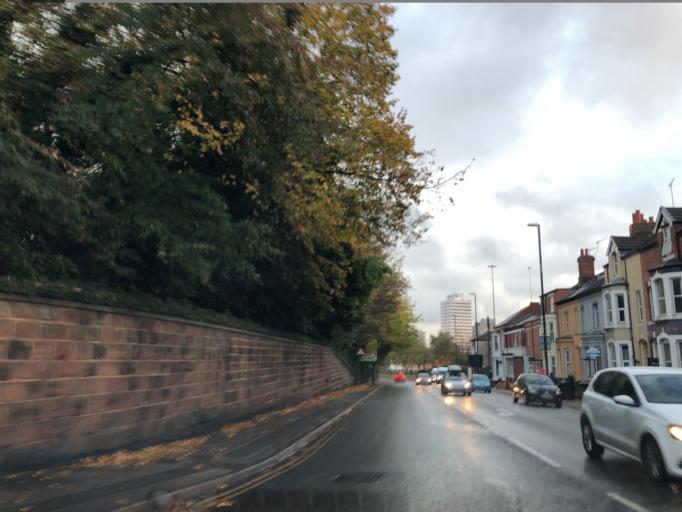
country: GB
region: England
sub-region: Coventry
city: Coventry
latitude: 52.4103
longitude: -1.5210
